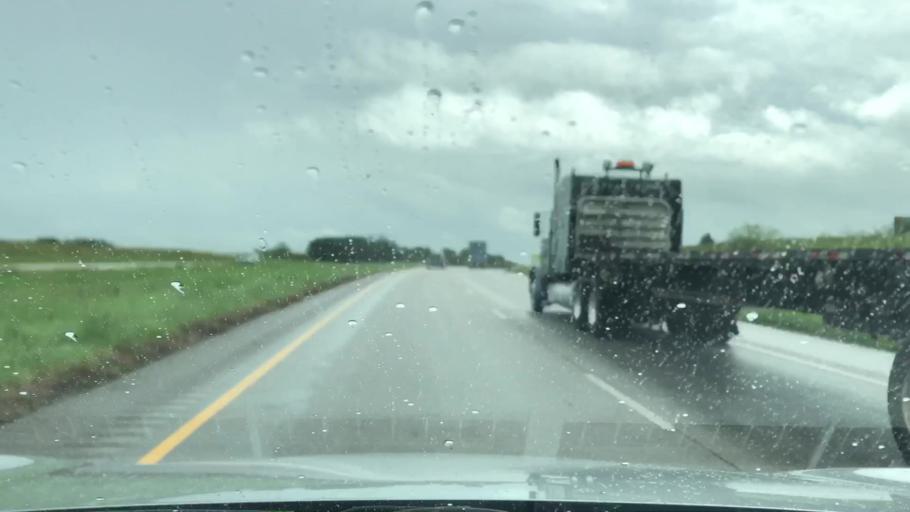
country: US
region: Texas
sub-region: Fayette County
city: Schulenburg
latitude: 29.6964
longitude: -96.8569
